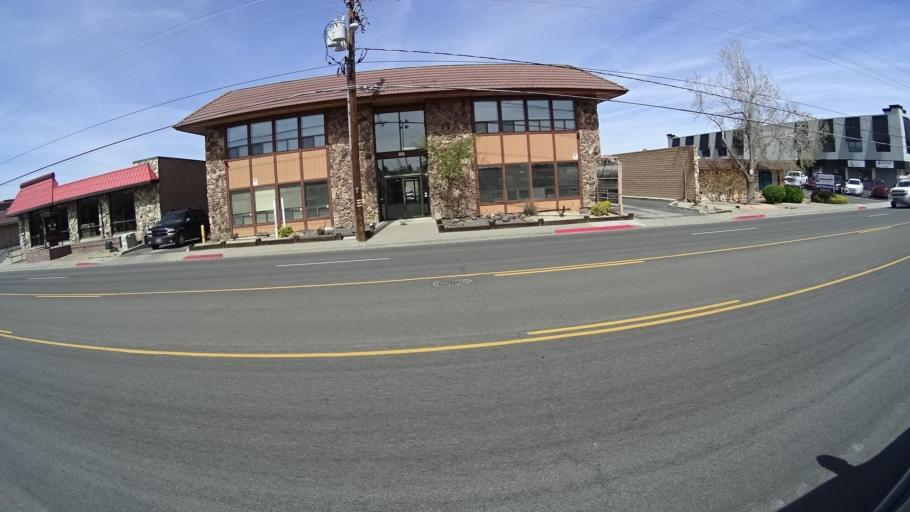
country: US
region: Nevada
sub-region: Washoe County
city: Reno
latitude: 39.4911
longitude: -119.8009
